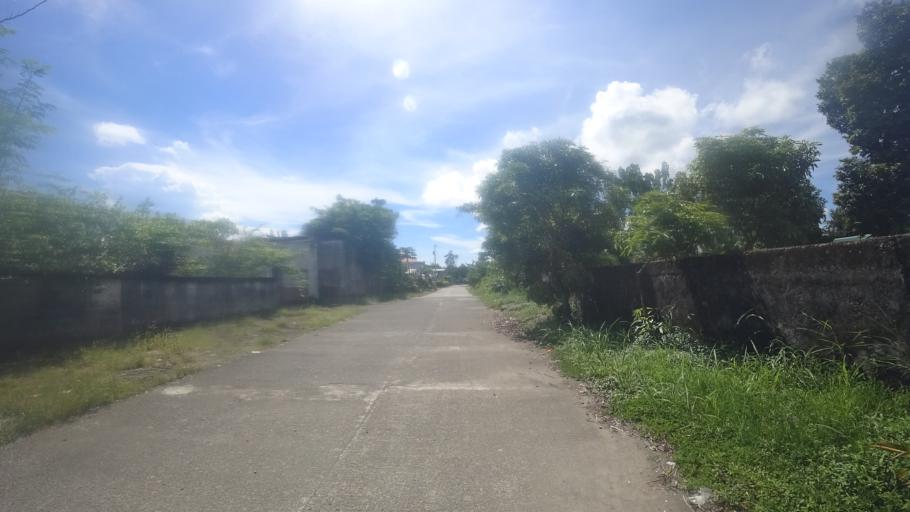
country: PH
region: Eastern Visayas
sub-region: Province of Leyte
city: Pastrana
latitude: 11.1537
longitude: 124.8592
